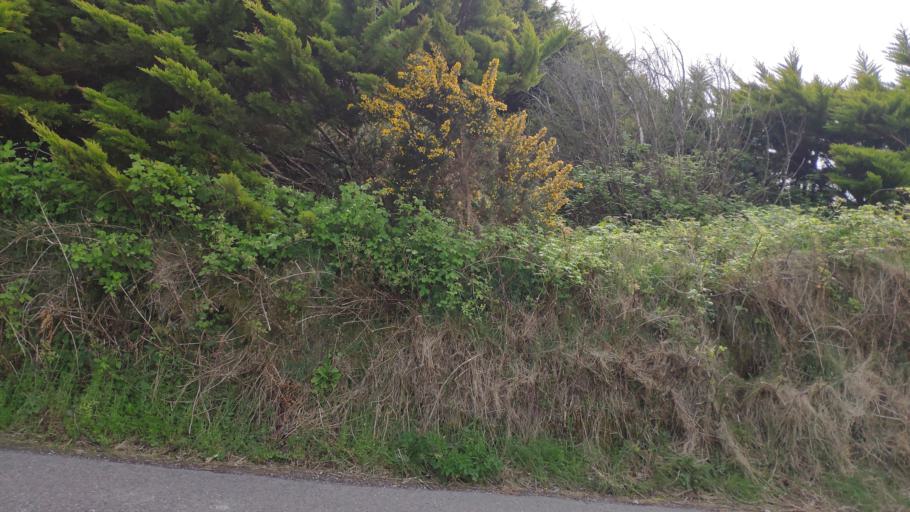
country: IE
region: Munster
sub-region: County Cork
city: Blarney
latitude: 51.9847
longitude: -8.5121
